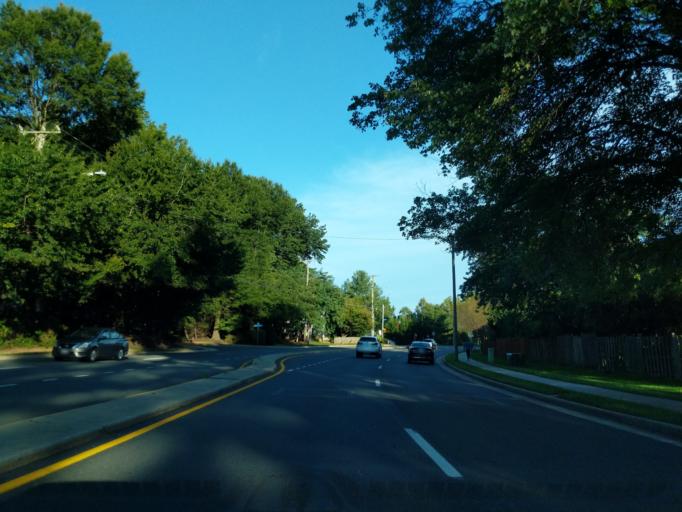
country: US
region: Virginia
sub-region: Fairfax County
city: Oakton
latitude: 38.8761
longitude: -77.2857
